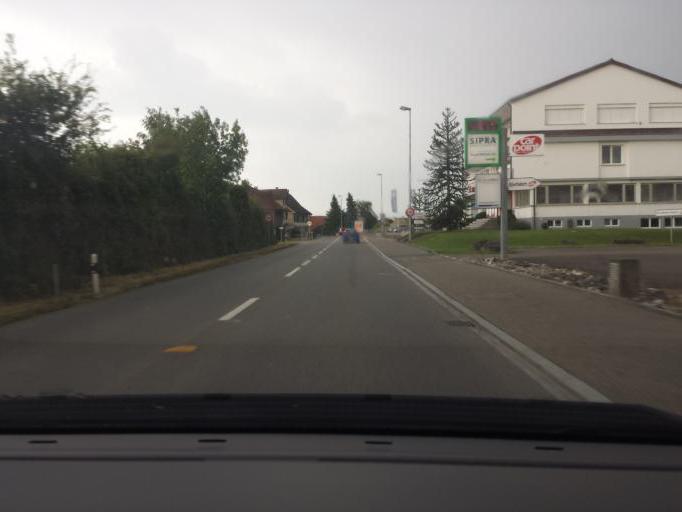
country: CH
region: Thurgau
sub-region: Arbon District
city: Salmsach
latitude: 47.5738
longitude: 9.3614
